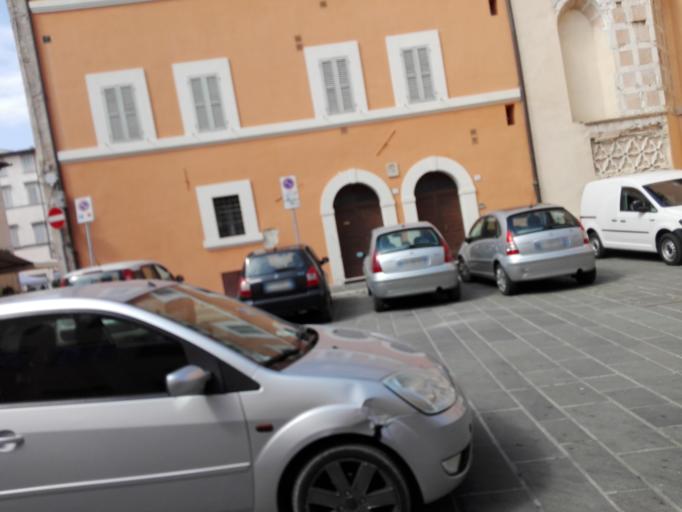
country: IT
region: Umbria
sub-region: Provincia di Perugia
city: Foligno
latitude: 42.9563
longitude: 12.7040
